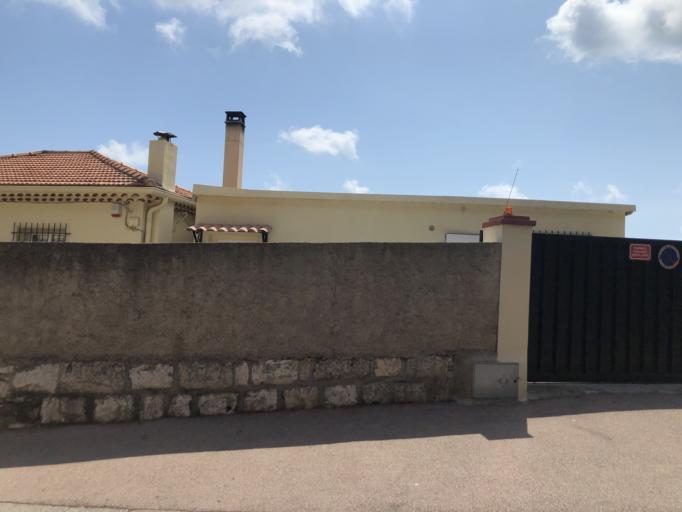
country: FR
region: Provence-Alpes-Cote d'Azur
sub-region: Departement des Alpes-Maritimes
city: Cap-d'Ail
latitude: 43.7220
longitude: 7.4027
